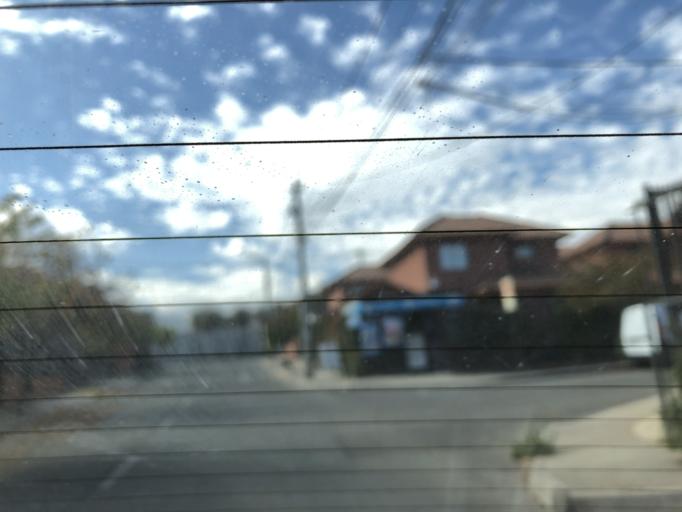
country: CL
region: Santiago Metropolitan
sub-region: Provincia de Cordillera
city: Puente Alto
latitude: -33.5764
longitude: -70.5406
